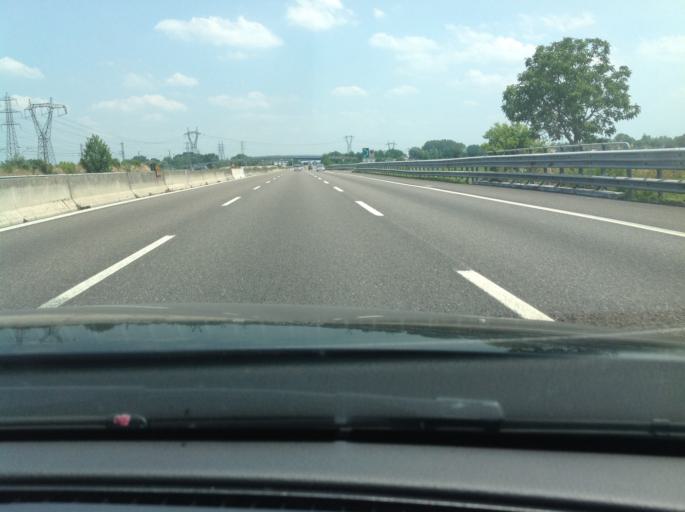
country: IT
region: Emilia-Romagna
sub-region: Provincia di Piacenza
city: Roveleto
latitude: 44.9892
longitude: 9.8425
